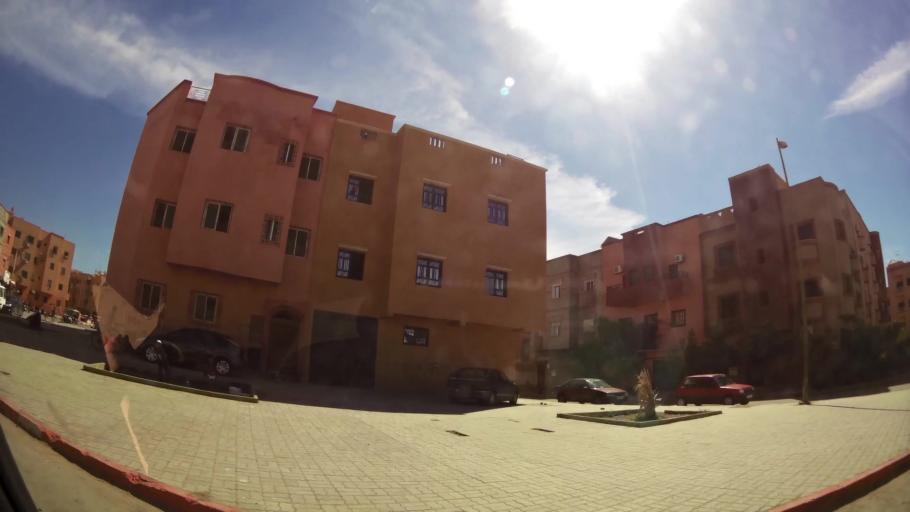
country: MA
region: Marrakech-Tensift-Al Haouz
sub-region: Marrakech
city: Marrakesh
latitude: 31.6792
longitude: -8.0189
